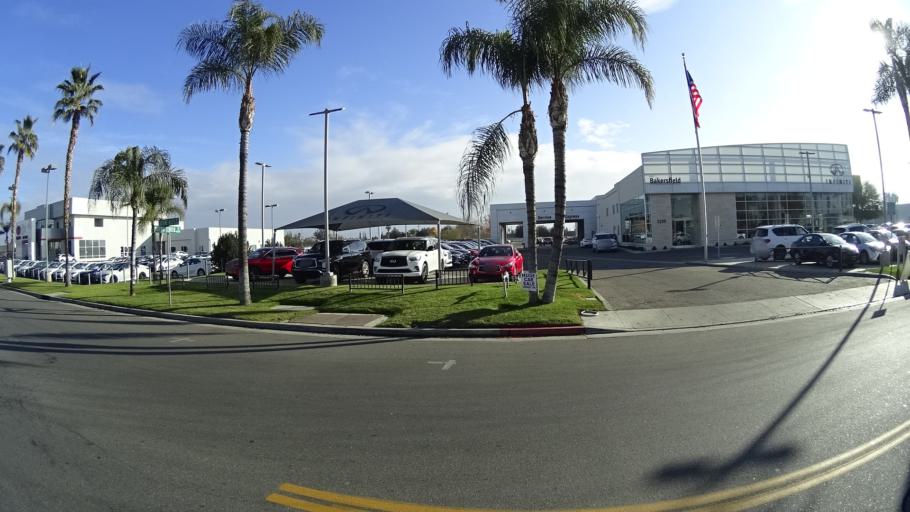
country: US
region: California
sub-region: Kern County
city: Greenfield
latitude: 35.3070
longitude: -119.0355
